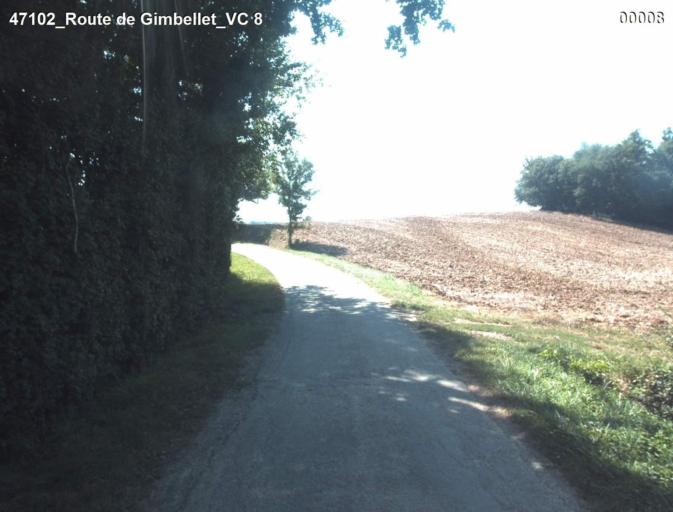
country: FR
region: Aquitaine
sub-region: Departement du Lot-et-Garonne
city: Laplume
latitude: 44.0471
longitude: 0.4457
